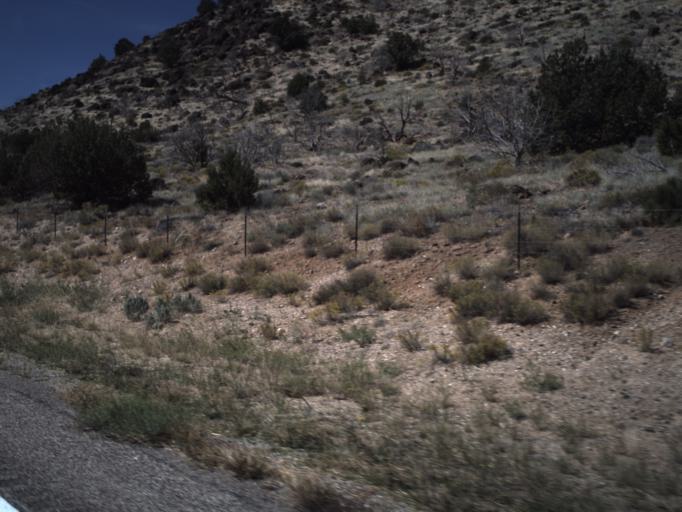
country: US
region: Utah
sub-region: Washington County
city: Ivins
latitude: 37.3730
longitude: -113.6593
